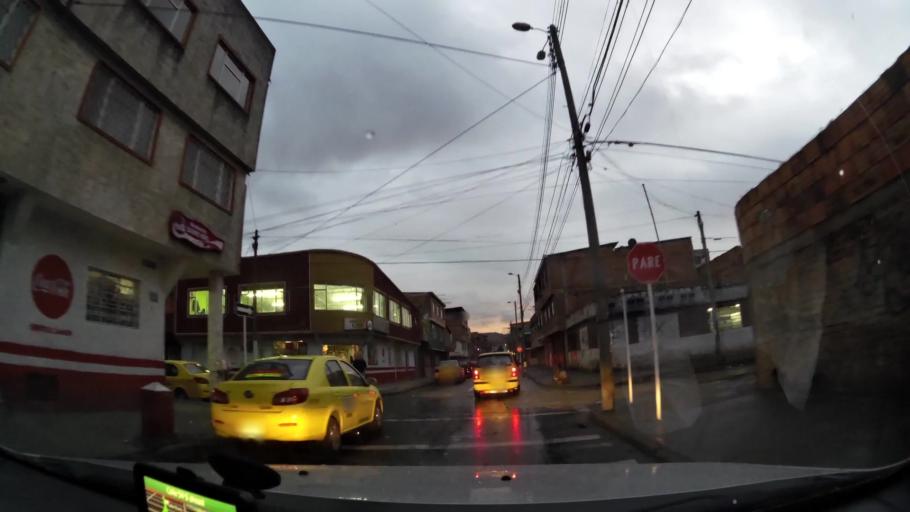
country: CO
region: Bogota D.C.
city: Bogota
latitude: 4.5828
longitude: -74.1405
